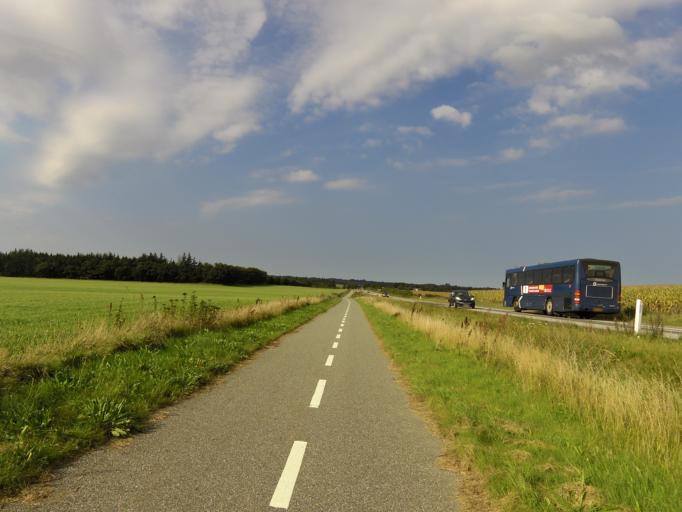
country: DK
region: South Denmark
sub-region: Vejen Kommune
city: Vejen
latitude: 55.4348
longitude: 9.1415
